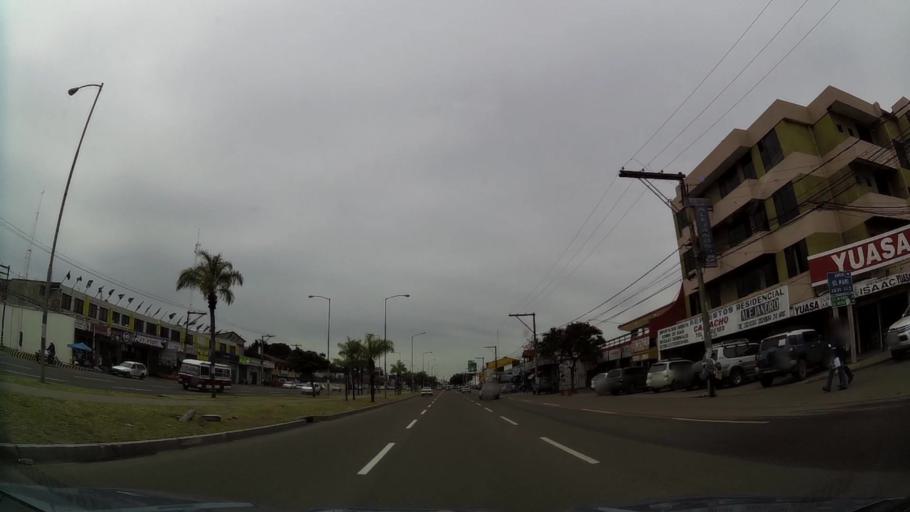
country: BO
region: Santa Cruz
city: Santa Cruz de la Sierra
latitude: -17.8004
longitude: -63.1952
